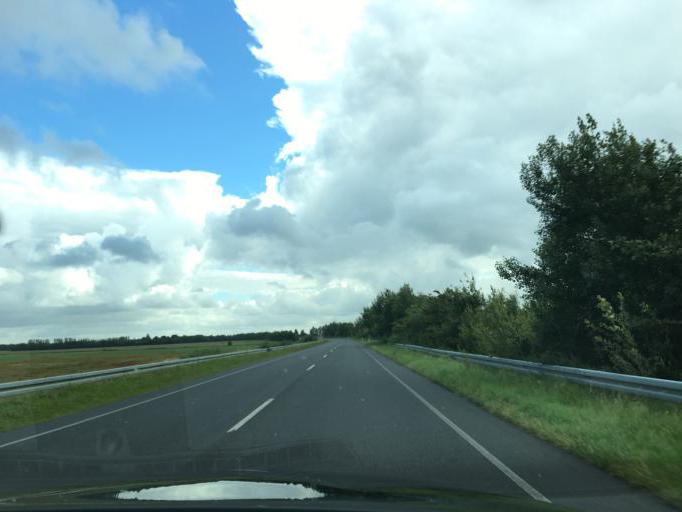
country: DK
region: South Denmark
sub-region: Varde Kommune
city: Olgod
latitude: 55.7909
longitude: 8.6266
